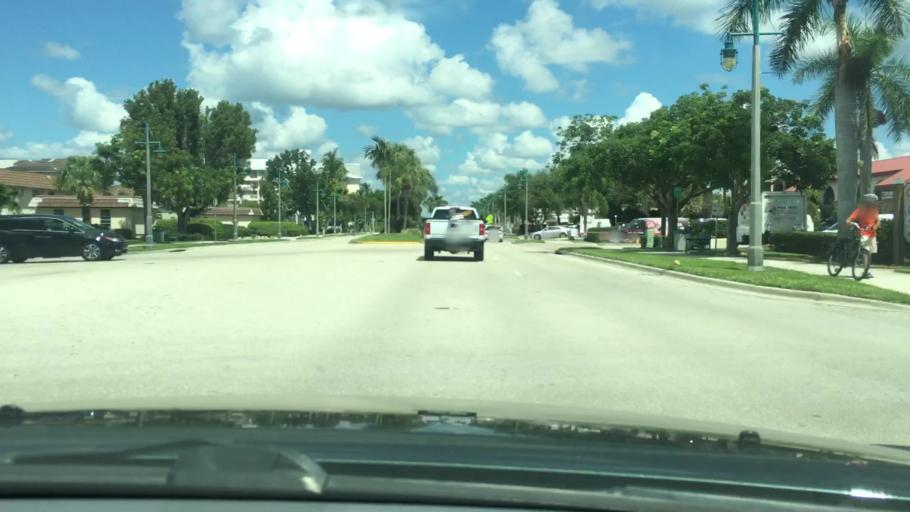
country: US
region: Florida
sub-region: Collier County
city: Marco
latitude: 25.9420
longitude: -81.7326
